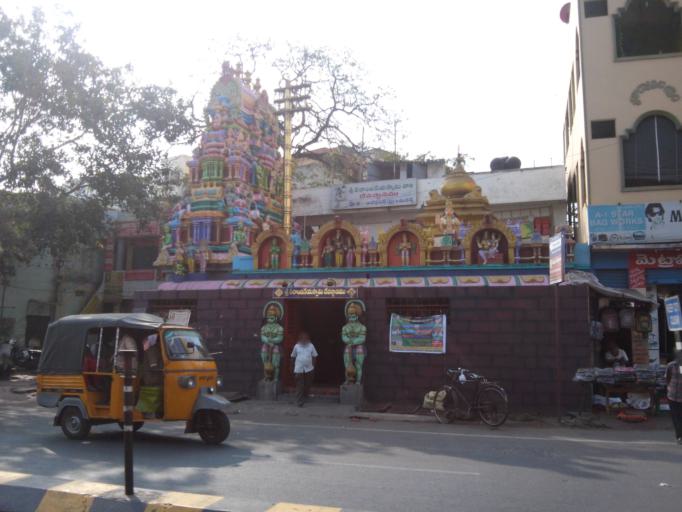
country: IN
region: Andhra Pradesh
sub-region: Krishna
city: Vijayawada
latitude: 16.5153
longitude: 80.6367
